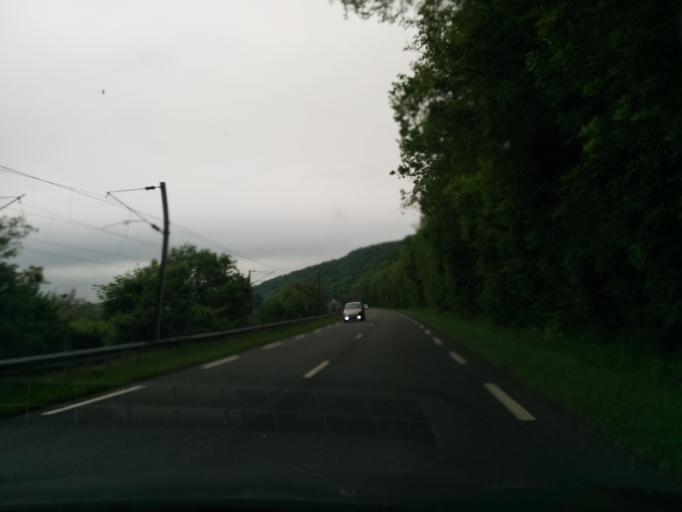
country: FR
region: Ile-de-France
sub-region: Departement des Yvelines
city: Bennecourt
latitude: 49.0391
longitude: 1.5380
